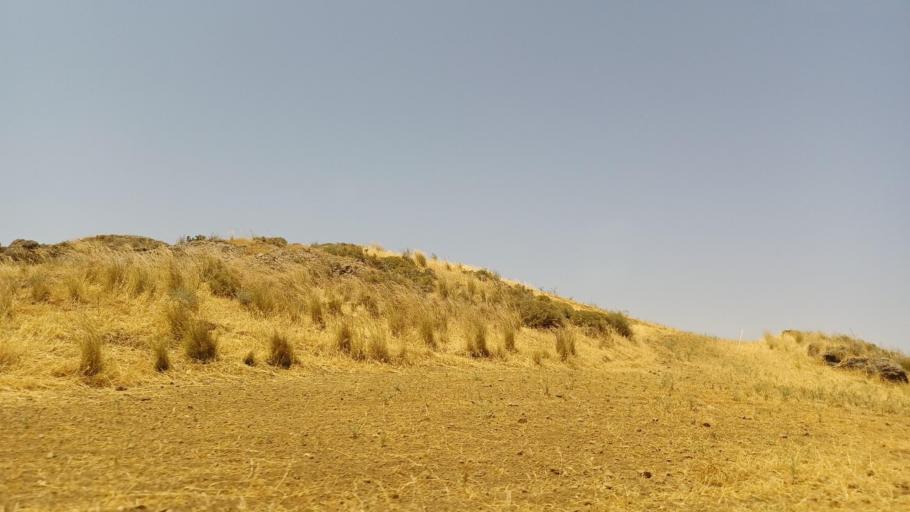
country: CY
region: Larnaka
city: Troulloi
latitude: 35.0223
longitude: 33.6359
